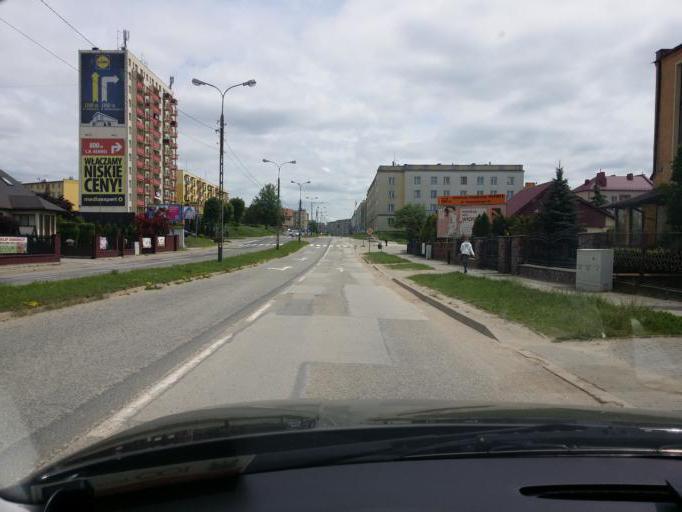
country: PL
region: Swietokrzyskie
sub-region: Powiat skarzyski
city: Skarzysko-Kamienna
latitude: 51.1183
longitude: 20.8521
